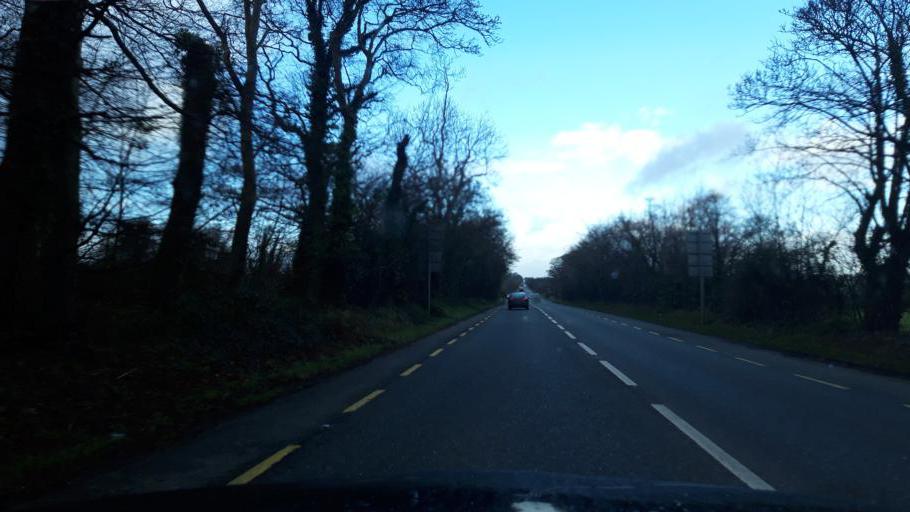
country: IE
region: Leinster
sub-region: An Mhi
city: Ashbourne
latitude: 53.5330
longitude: -6.4216
